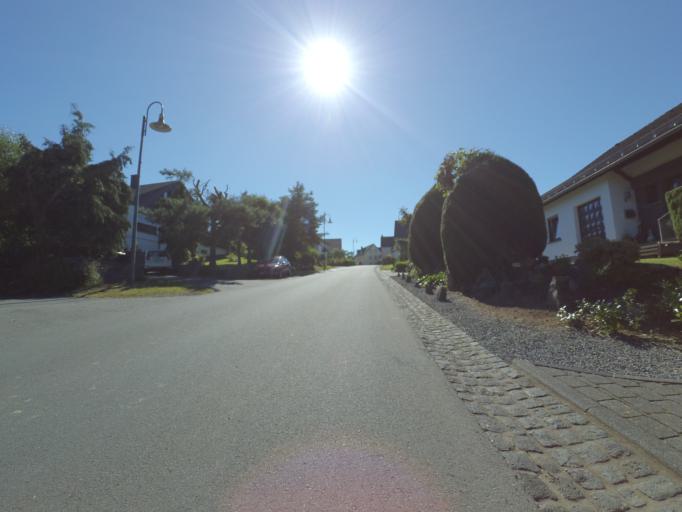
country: DE
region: Rheinland-Pfalz
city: Daun
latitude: 50.2062
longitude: 6.8460
